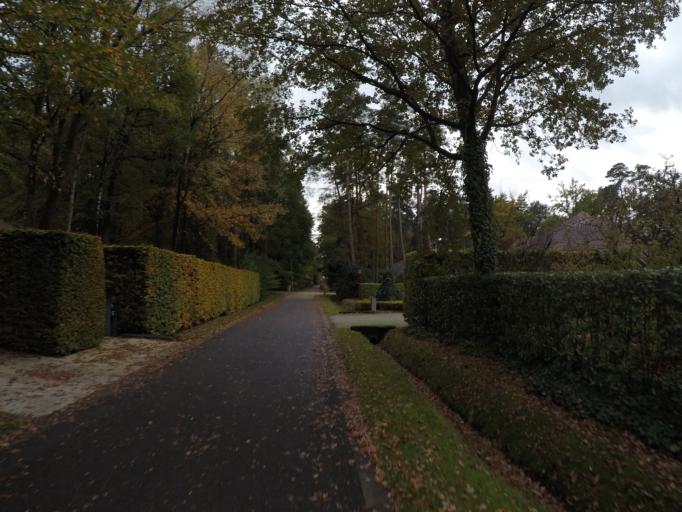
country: BE
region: Flanders
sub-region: Provincie Antwerpen
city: Zoersel
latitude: 51.2598
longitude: 4.6817
